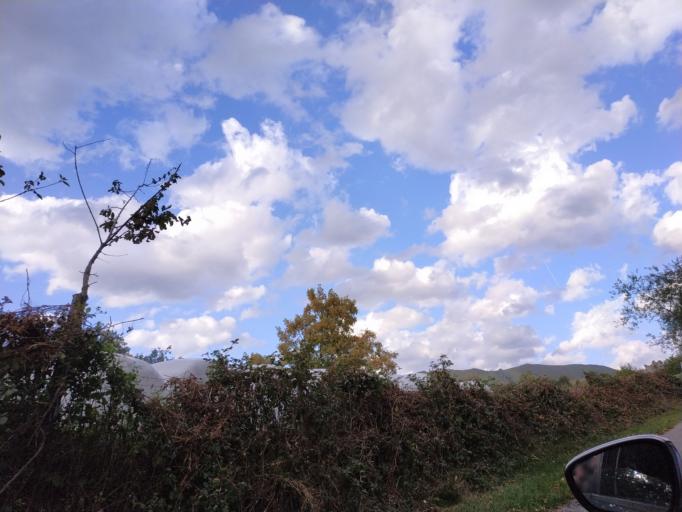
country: ES
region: Castille and Leon
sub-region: Provincia de Leon
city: Candin
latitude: 42.8588
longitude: -6.8675
